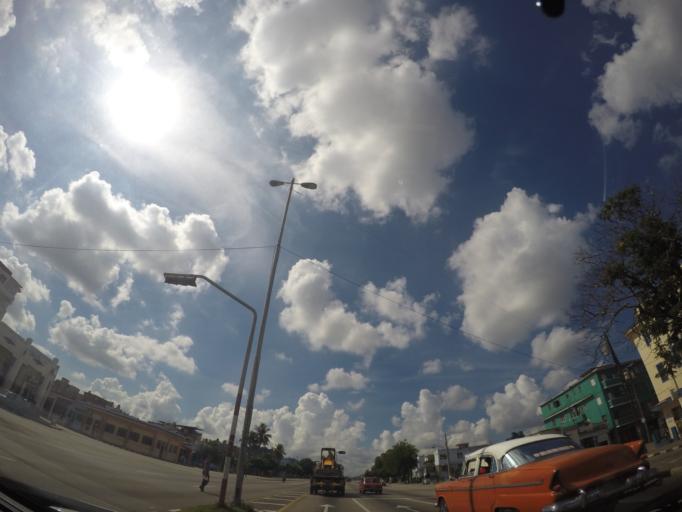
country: CU
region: La Habana
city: Cerro
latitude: 23.1110
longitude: -82.4181
